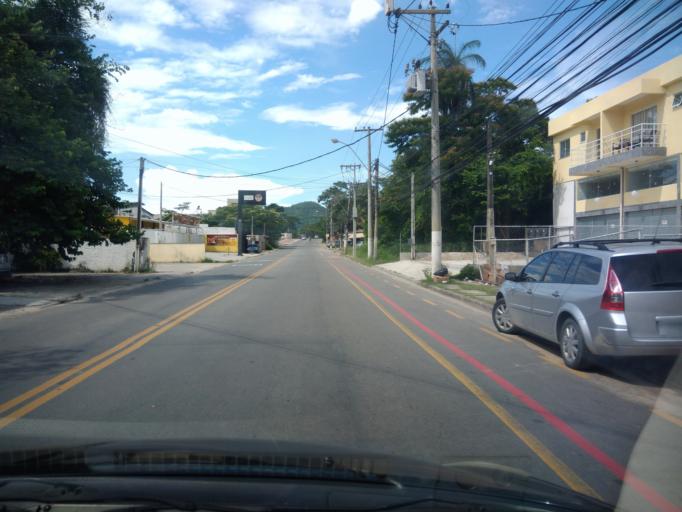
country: BR
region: Rio de Janeiro
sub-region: Niteroi
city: Niteroi
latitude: -22.9417
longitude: -43.0178
